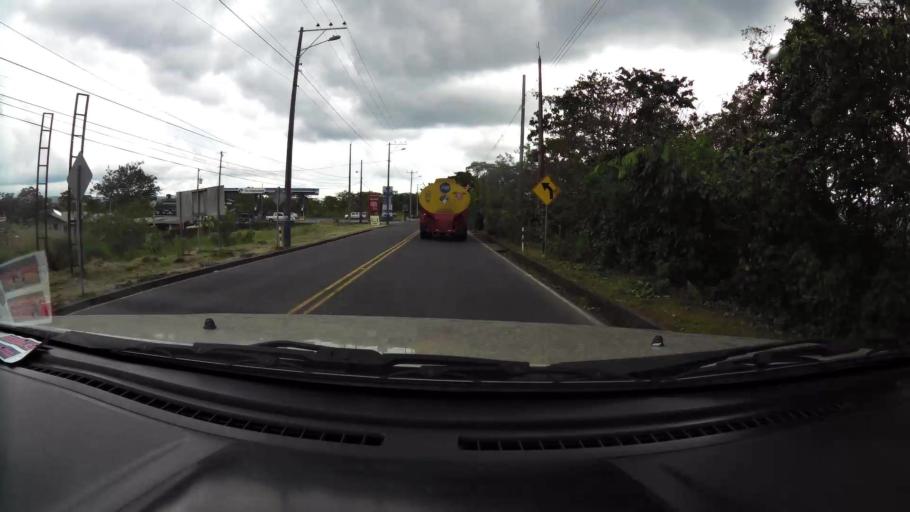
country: EC
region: Pastaza
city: Puyo
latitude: -1.4559
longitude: -78.1208
